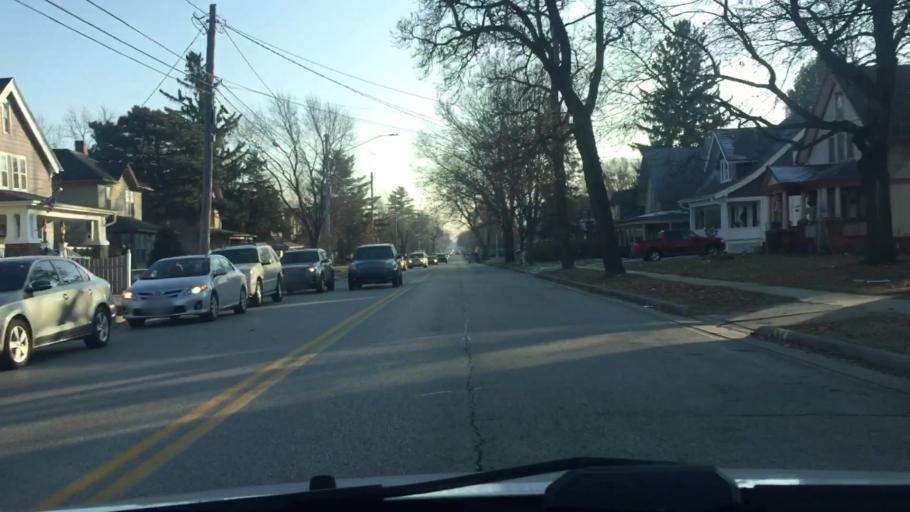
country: US
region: Wisconsin
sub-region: Waukesha County
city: Oconomowoc
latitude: 43.1071
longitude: -88.4959
